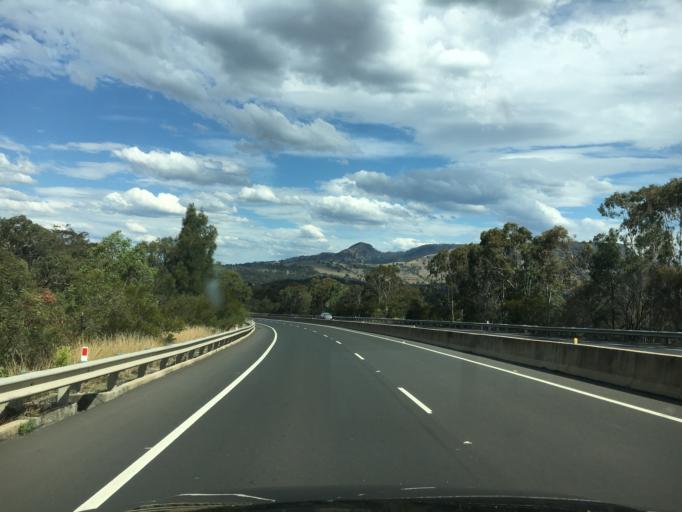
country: AU
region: New South Wales
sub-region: Liverpool Plains
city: Quirindi
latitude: -31.7470
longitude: 150.8069
